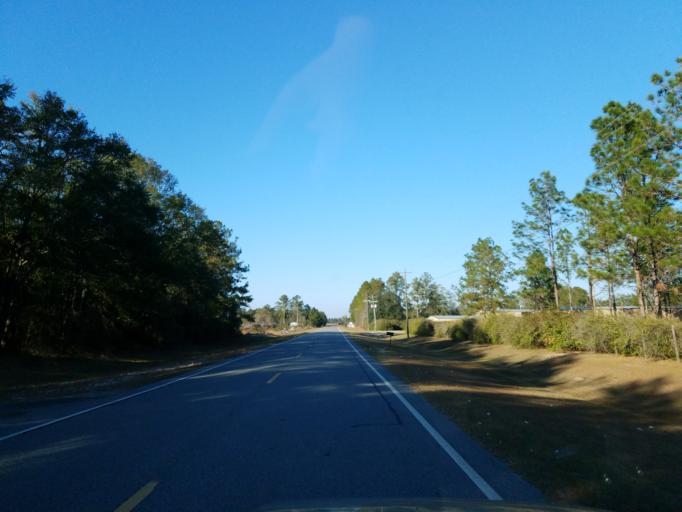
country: US
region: Georgia
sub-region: Echols County
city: Statenville
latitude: 30.6642
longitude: -83.0610
